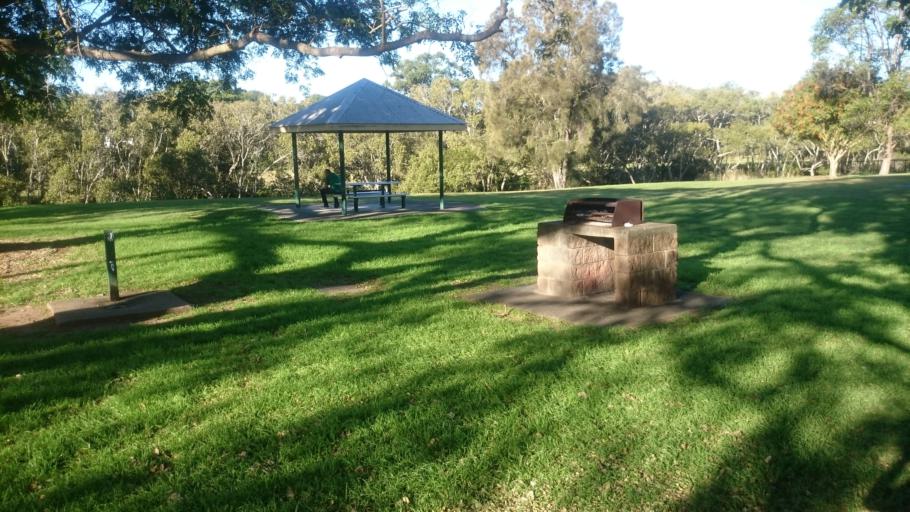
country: AU
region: Queensland
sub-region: Brisbane
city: Manly West
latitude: -27.4717
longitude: 153.1851
